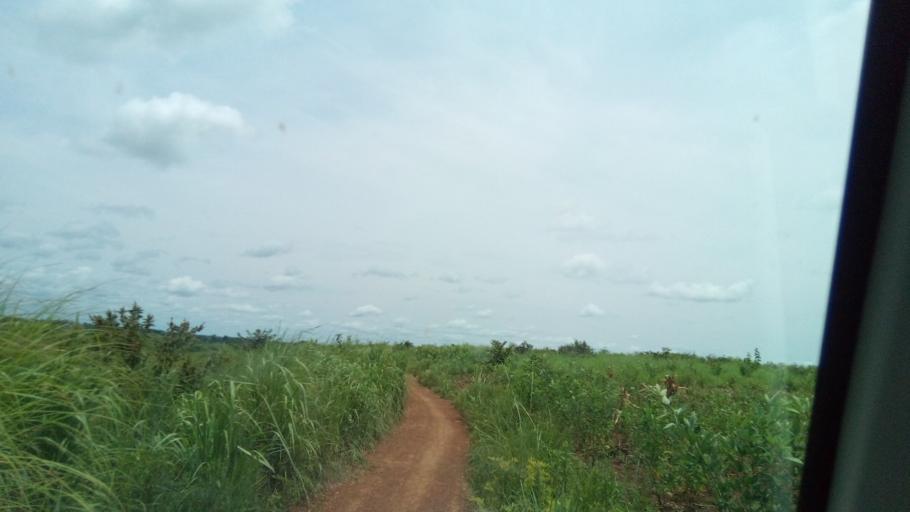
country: AO
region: Zaire
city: Mbanza Congo
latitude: -5.7881
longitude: 13.9920
